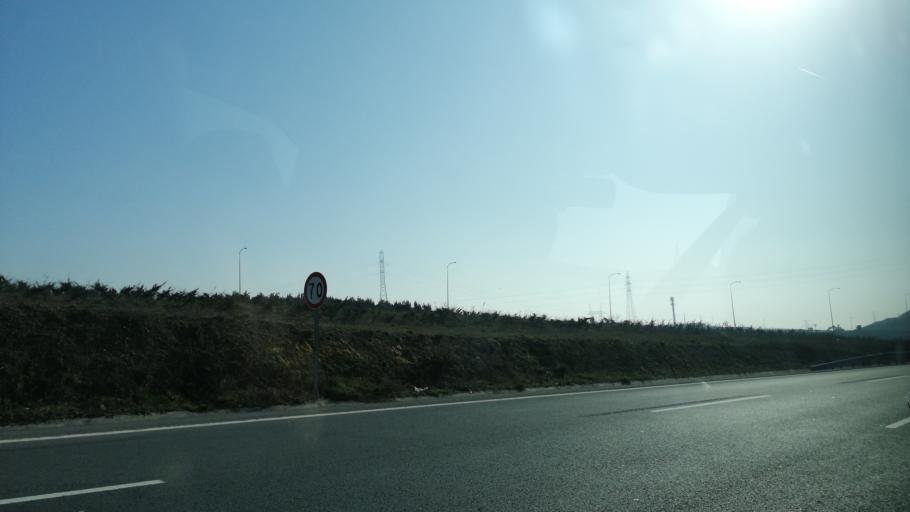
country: TR
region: Kocaeli
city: Tavsanli
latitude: 40.7978
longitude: 29.5085
